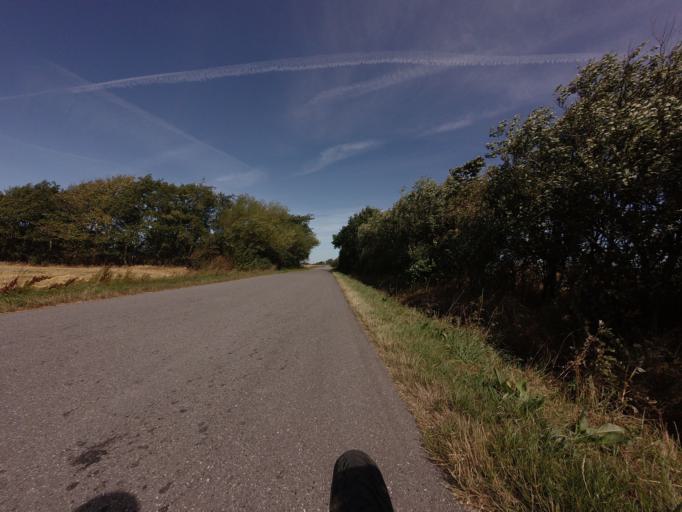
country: DK
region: North Denmark
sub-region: Bronderslev Kommune
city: Bronderslev
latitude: 57.3194
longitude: 9.8151
